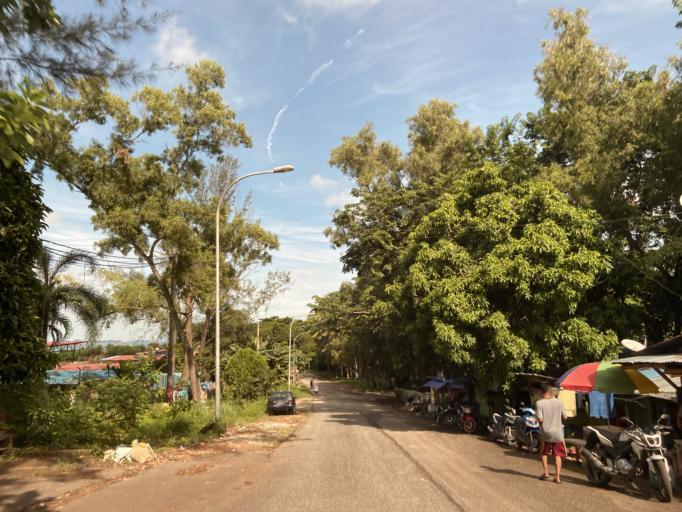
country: SG
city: Singapore
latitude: 1.1585
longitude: 104.0078
